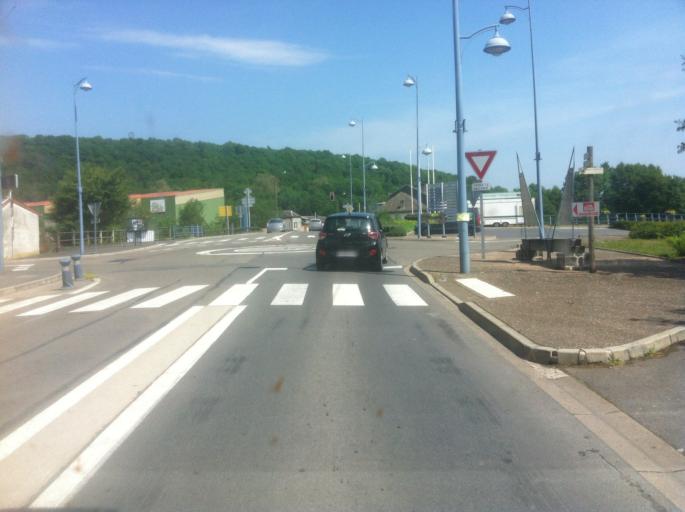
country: FR
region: Champagne-Ardenne
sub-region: Departement des Ardennes
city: Vireux-Wallerand
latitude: 50.0871
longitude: 4.7252
